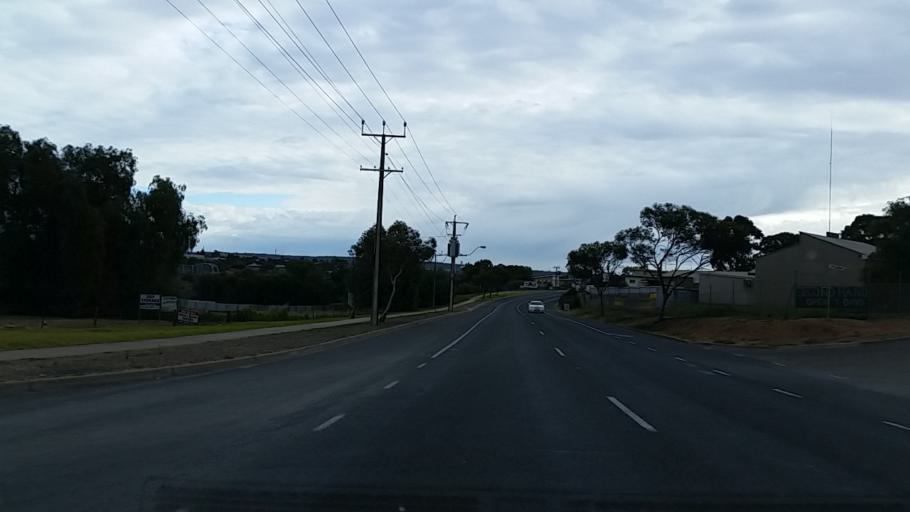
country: AU
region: South Australia
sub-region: Murray Bridge
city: Murray Bridge
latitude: -35.1128
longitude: 139.2897
